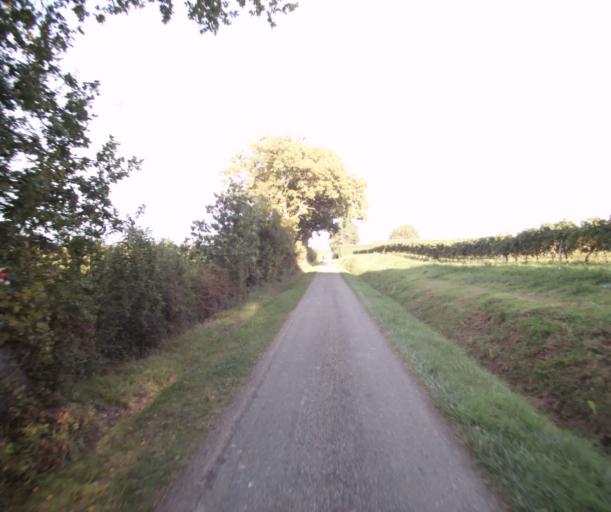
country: FR
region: Midi-Pyrenees
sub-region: Departement du Gers
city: Eauze
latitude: 43.8748
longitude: 0.0217
